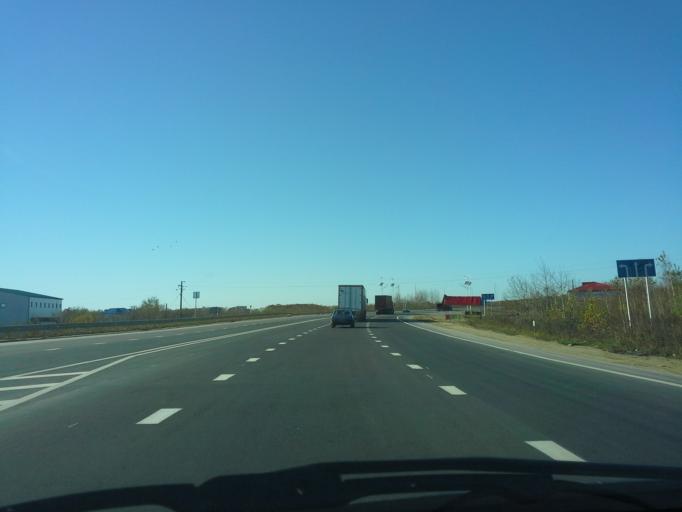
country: RU
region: Jewish Autonomous Oblast
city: Priamurskiy
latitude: 48.5186
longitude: 134.9122
